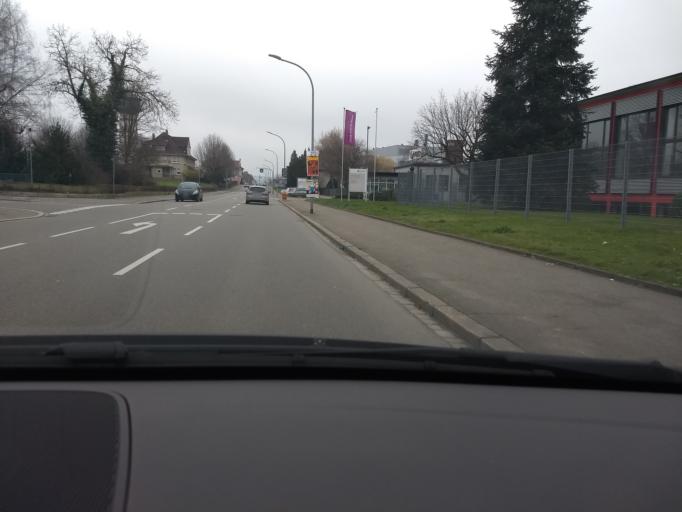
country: DE
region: Baden-Wuerttemberg
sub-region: Freiburg Region
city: Rheinfelden (Baden)
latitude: 47.5627
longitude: 7.7927
